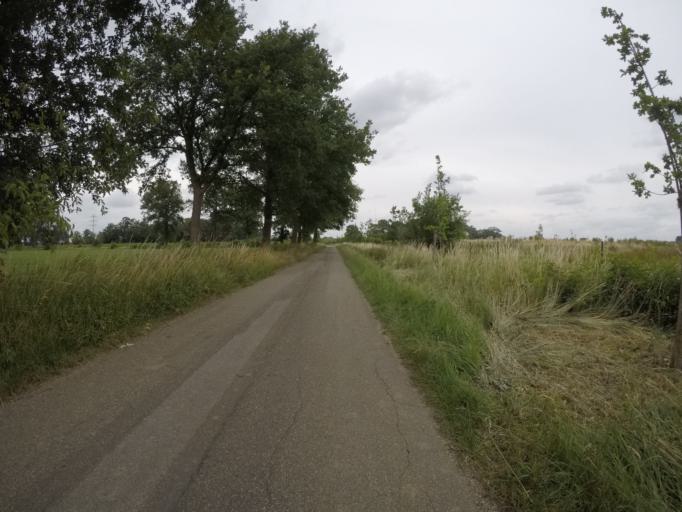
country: DE
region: North Rhine-Westphalia
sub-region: Regierungsbezirk Munster
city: Isselburg
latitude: 51.8483
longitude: 6.4496
